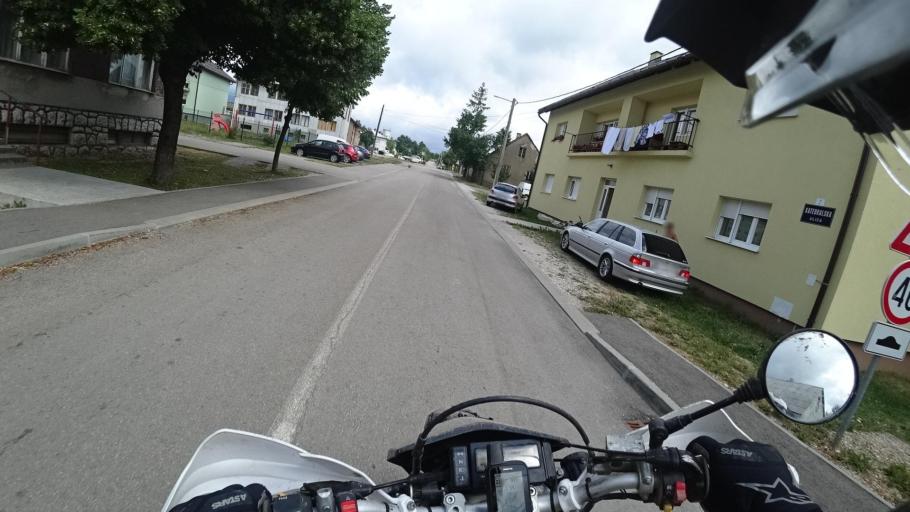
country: HR
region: Zadarska
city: Gracac
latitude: 44.5313
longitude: 15.7669
